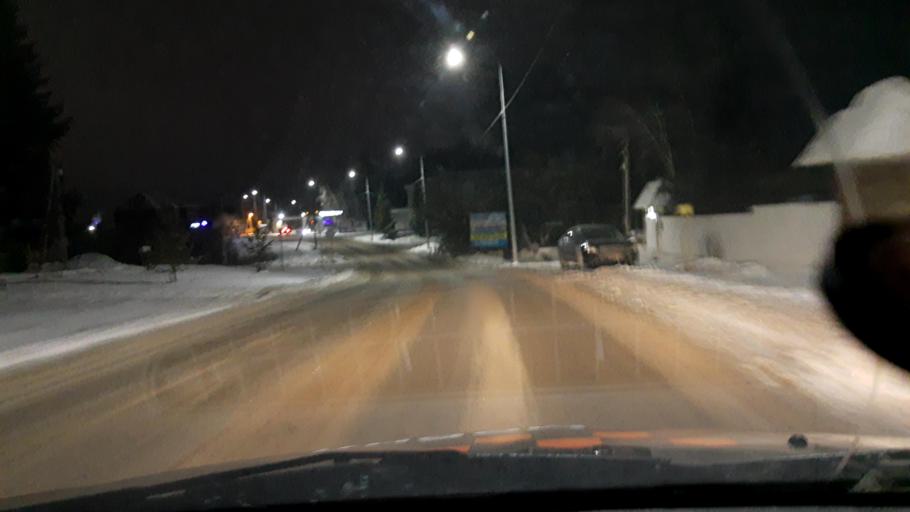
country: RU
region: Bashkortostan
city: Avdon
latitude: 54.5001
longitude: 55.8931
